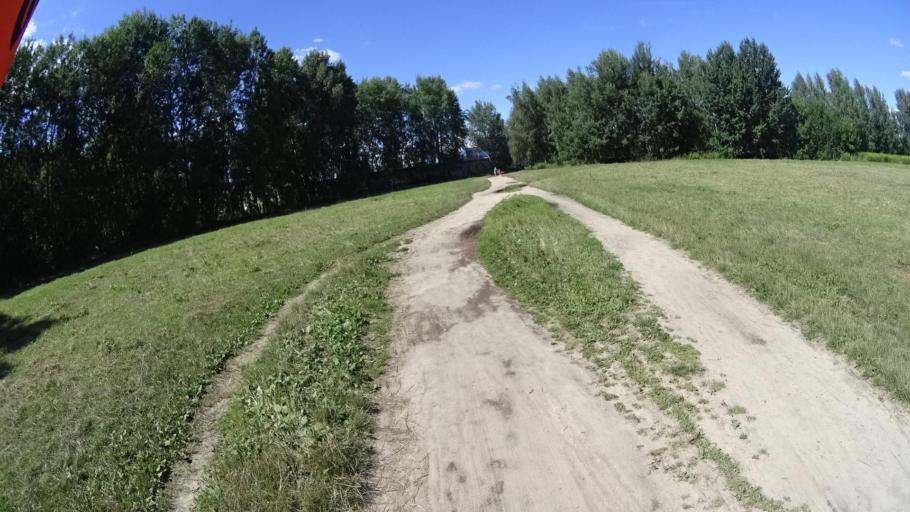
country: PL
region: Masovian Voivodeship
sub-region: Warszawa
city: Kabaty
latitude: 52.1243
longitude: 21.0743
